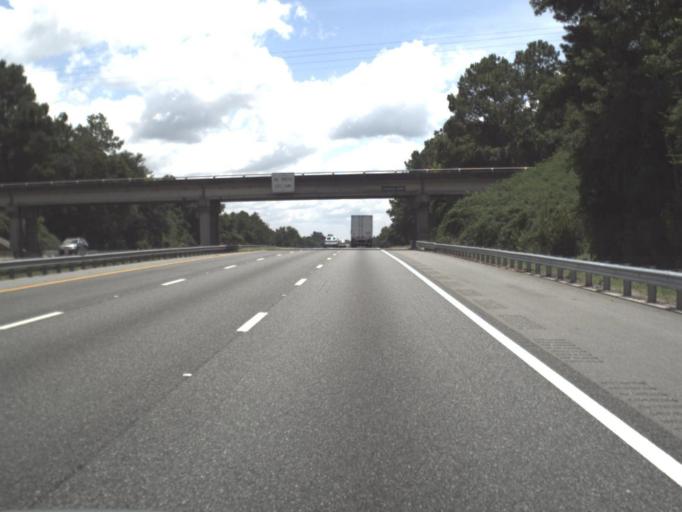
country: US
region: Florida
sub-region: Columbia County
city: Lake City
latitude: 30.0274
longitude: -82.6126
